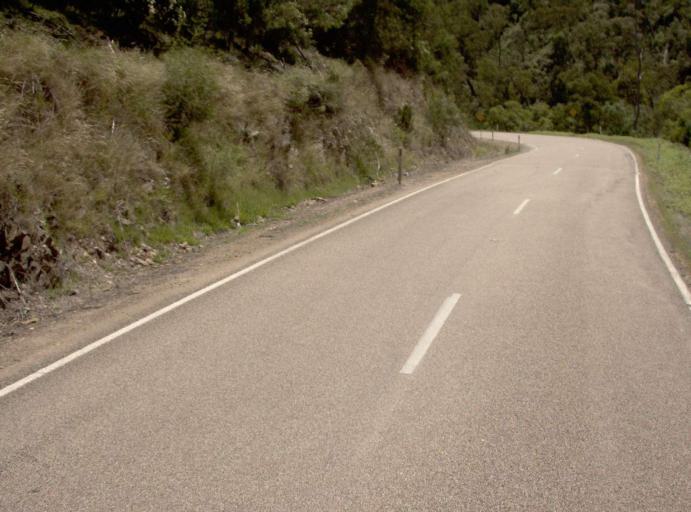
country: AU
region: Victoria
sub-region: East Gippsland
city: Lakes Entrance
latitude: -37.5309
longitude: 147.8534
